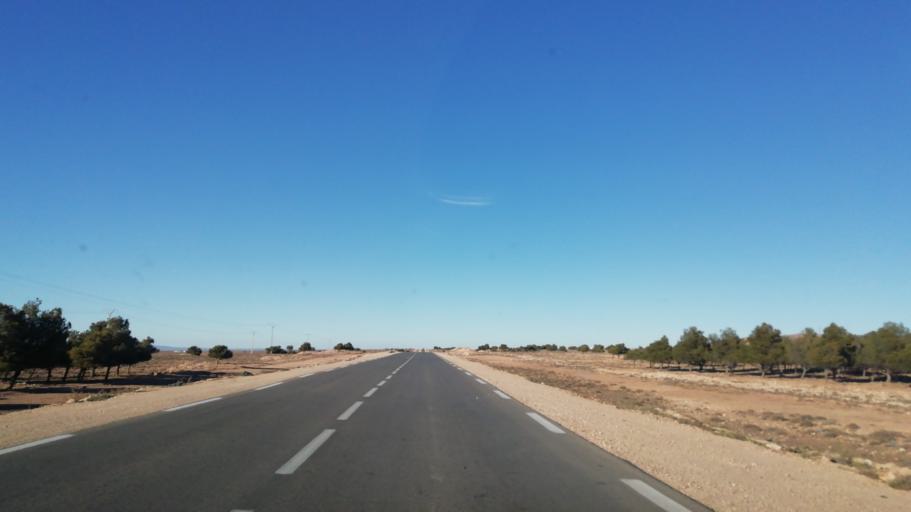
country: DZ
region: Tlemcen
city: Sebdou
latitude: 34.2457
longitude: -1.2572
